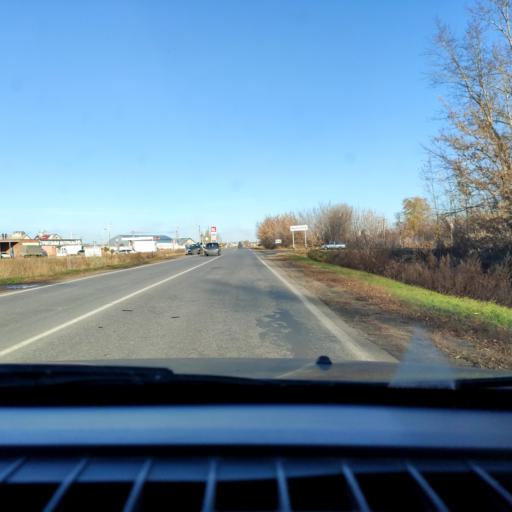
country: RU
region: Samara
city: Tol'yatti
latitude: 53.6315
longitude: 49.3025
